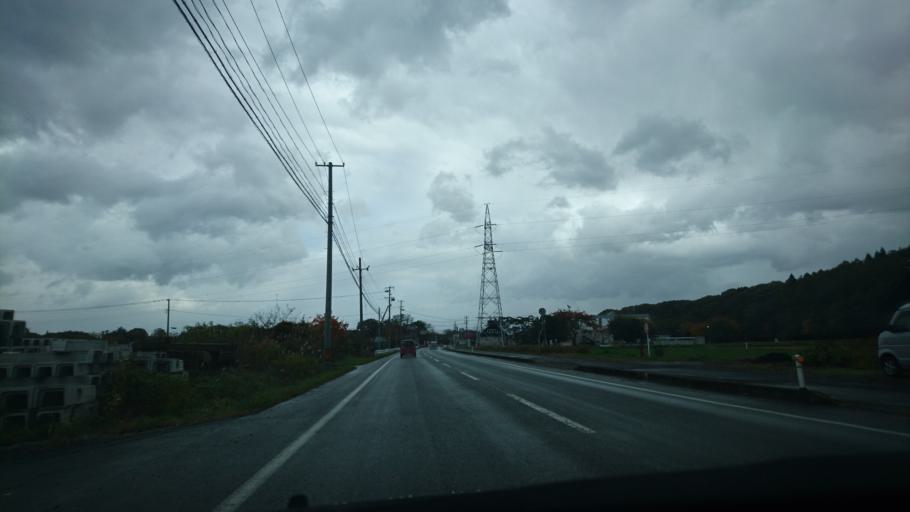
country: JP
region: Iwate
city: Shizukuishi
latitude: 39.6610
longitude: 140.9653
